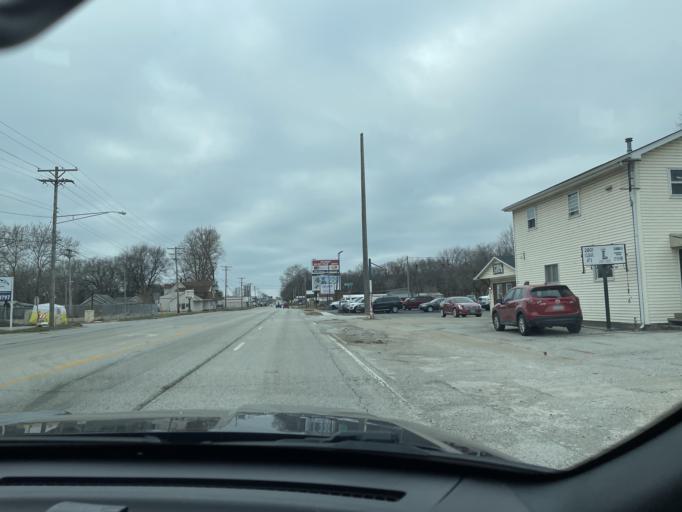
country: US
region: Illinois
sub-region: Sangamon County
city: Grandview
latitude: 39.8021
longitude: -89.6142
